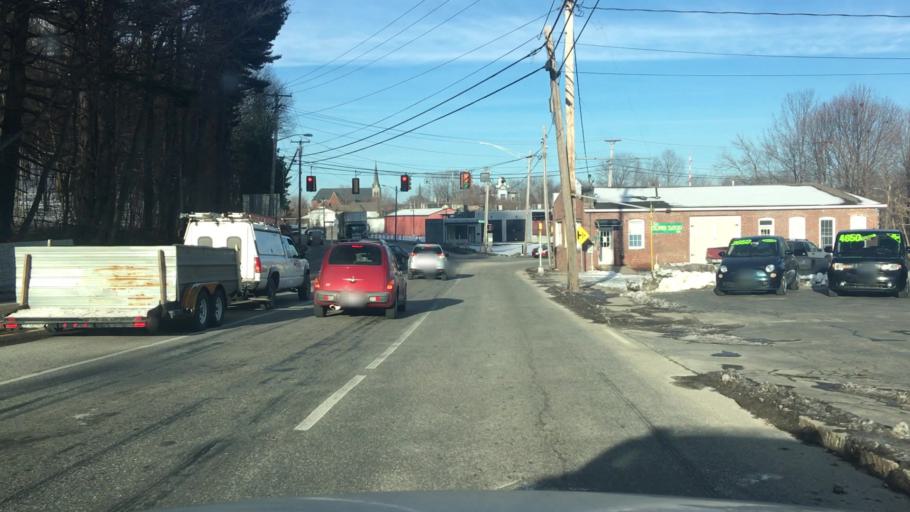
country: US
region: Maine
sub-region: Androscoggin County
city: Auburn
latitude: 44.0903
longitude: -70.2308
